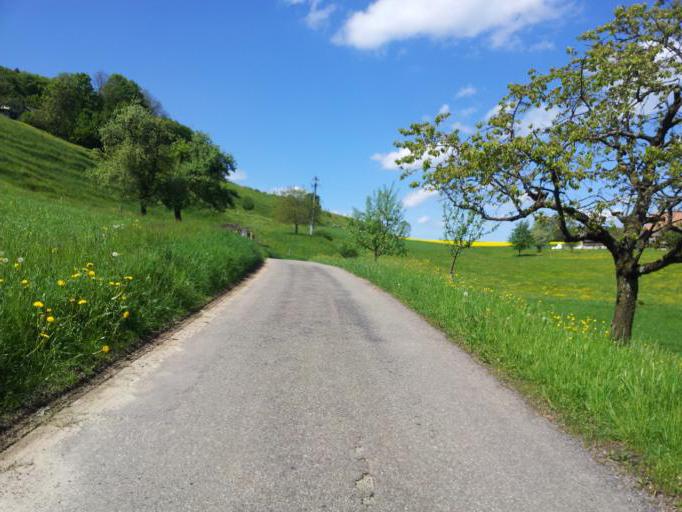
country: CH
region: Aargau
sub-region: Bezirk Bremgarten
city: Rudolfstetten
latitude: 47.3774
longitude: 8.3668
